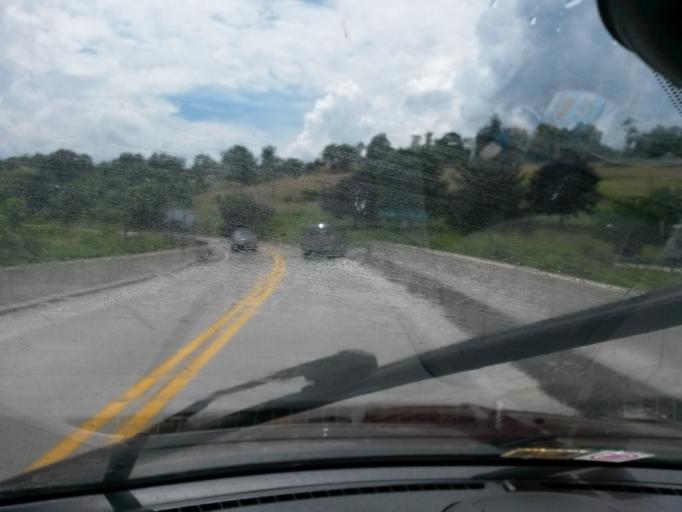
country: US
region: West Virginia
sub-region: Pendleton County
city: Franklin
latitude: 38.8054
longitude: -79.2765
